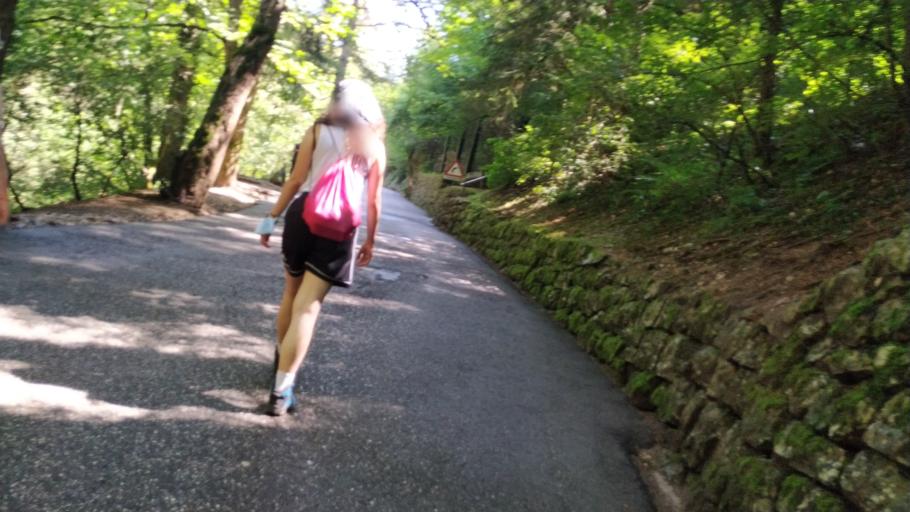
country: IT
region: Trentino-Alto Adige
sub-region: Provincia di Trento
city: Smarano
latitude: 46.3696
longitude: 11.1071
